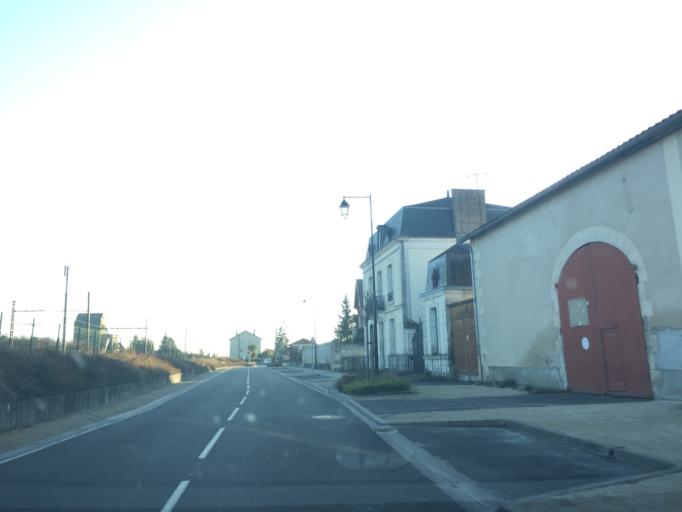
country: FR
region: Poitou-Charentes
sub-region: Departement de la Charente
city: Chalais
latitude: 45.2699
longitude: 0.0428
